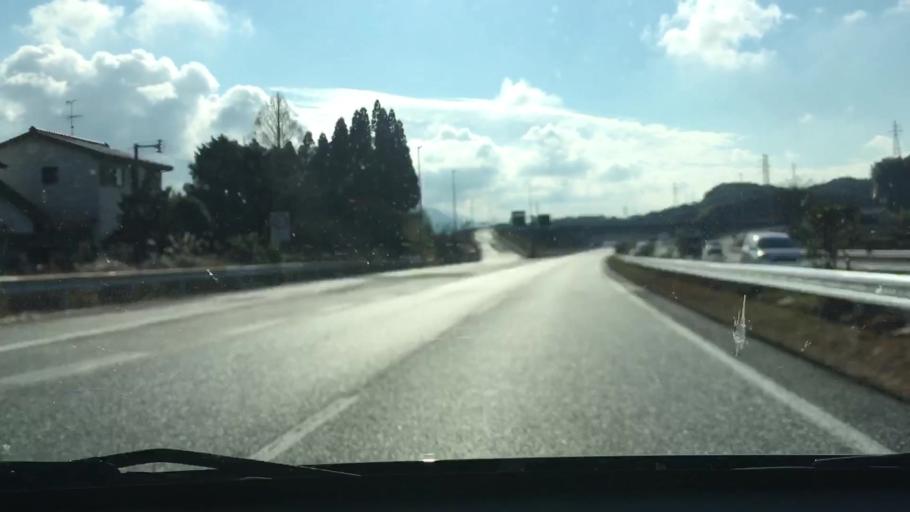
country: JP
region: Kumamoto
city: Matsubase
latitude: 32.5793
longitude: 130.7130
